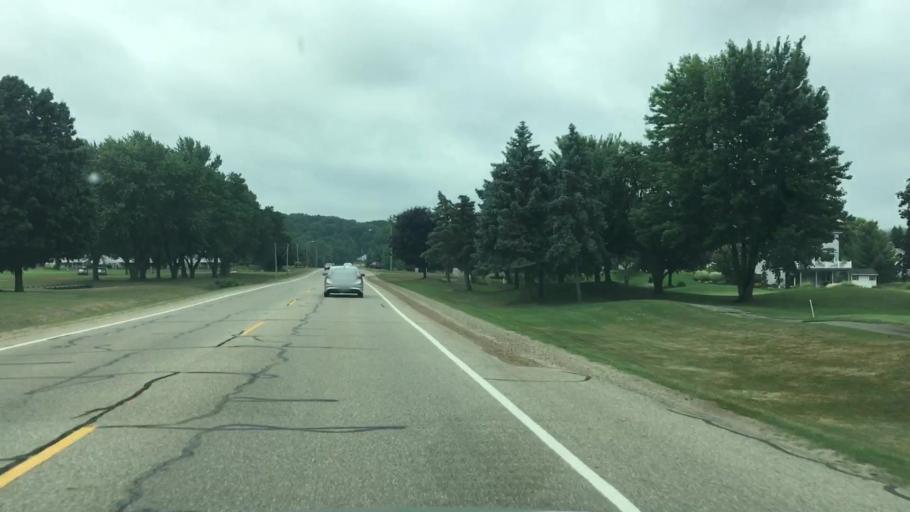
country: US
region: Michigan
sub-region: Ottawa County
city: Jenison
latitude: 42.8784
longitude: -85.8168
